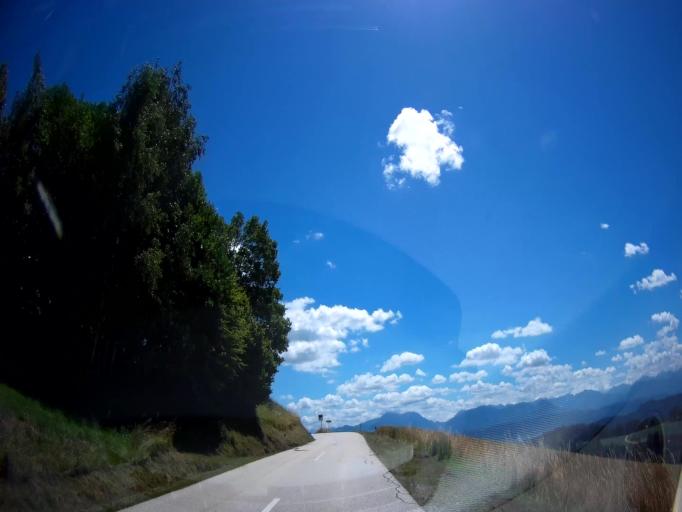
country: AT
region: Carinthia
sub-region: Politischer Bezirk Sankt Veit an der Glan
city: St. Georgen am Laengsee
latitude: 46.7202
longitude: 14.4223
